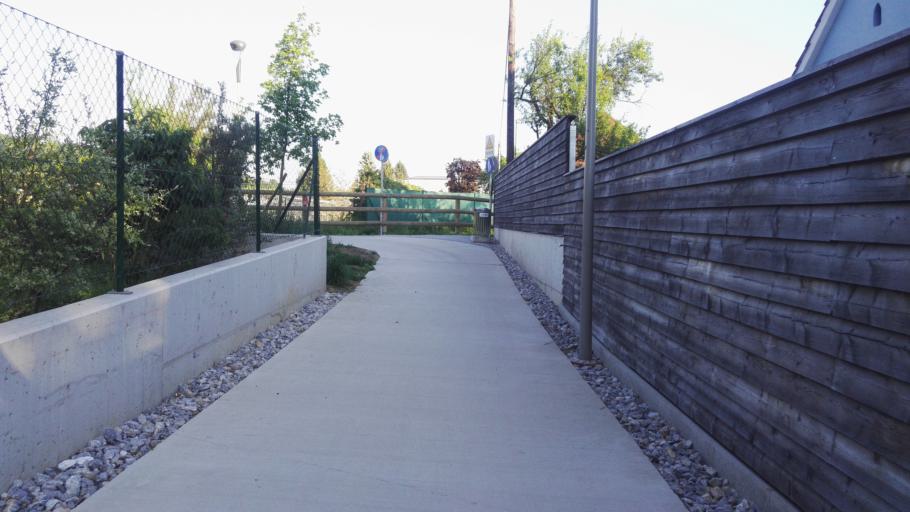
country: AT
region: Styria
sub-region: Graz Stadt
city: Graz
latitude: 47.0522
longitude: 15.4728
